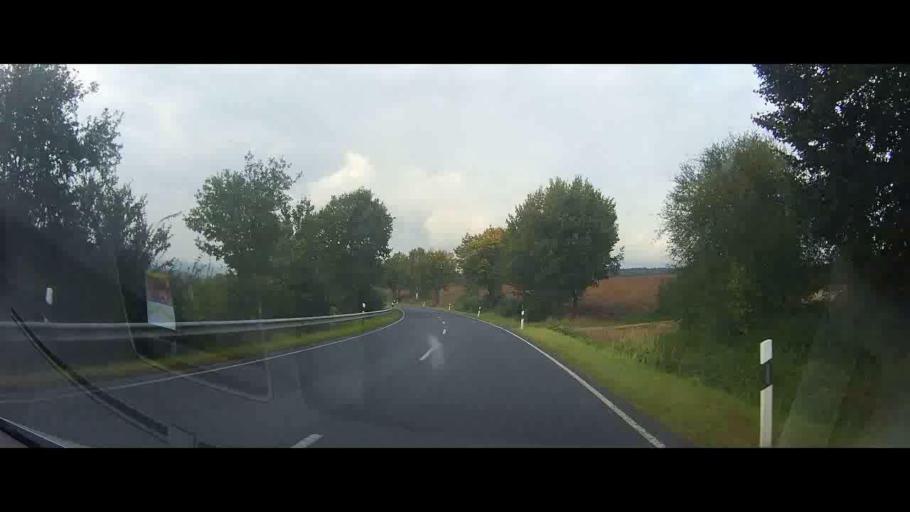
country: DE
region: Lower Saxony
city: Adelebsen
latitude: 51.5733
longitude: 9.7065
